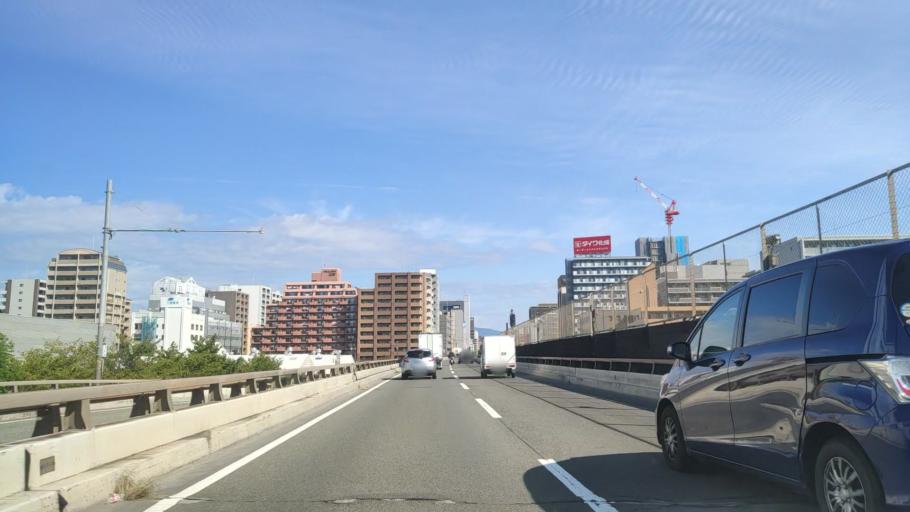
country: JP
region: Osaka
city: Suita
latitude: 34.7524
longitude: 135.4966
